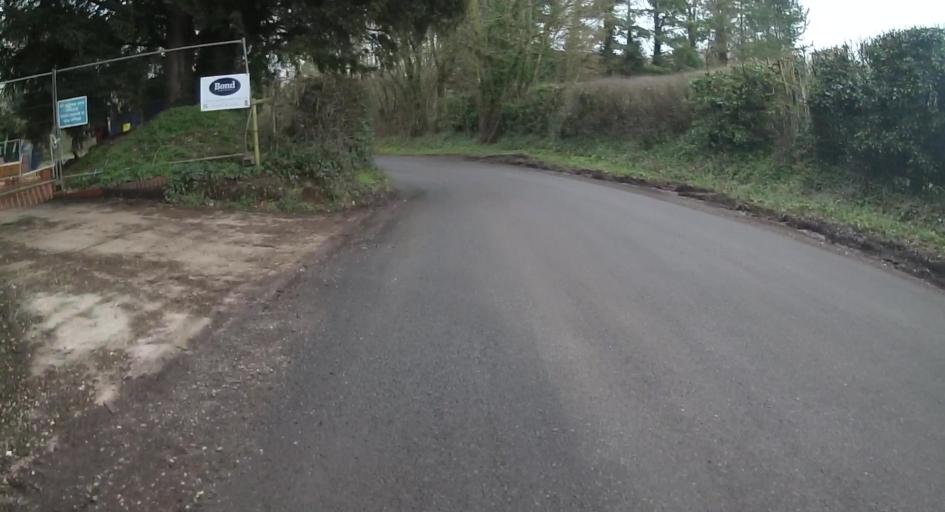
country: GB
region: England
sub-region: Hampshire
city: Kingsclere
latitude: 51.3311
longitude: -1.2827
